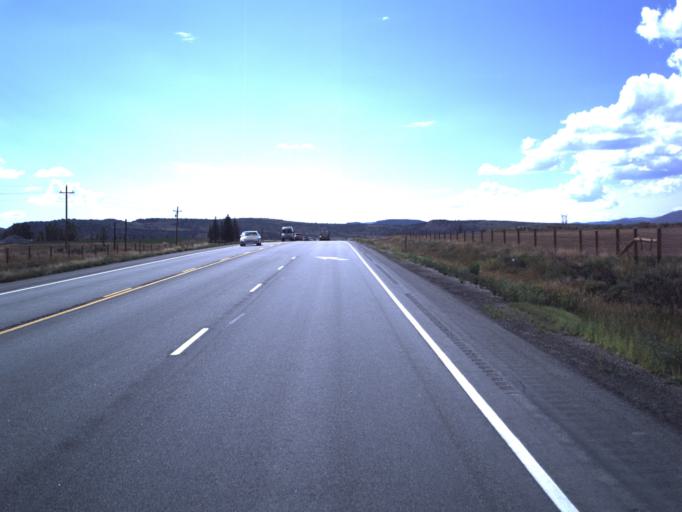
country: US
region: Utah
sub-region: Duchesne County
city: Duchesne
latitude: 40.2125
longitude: -110.8495
